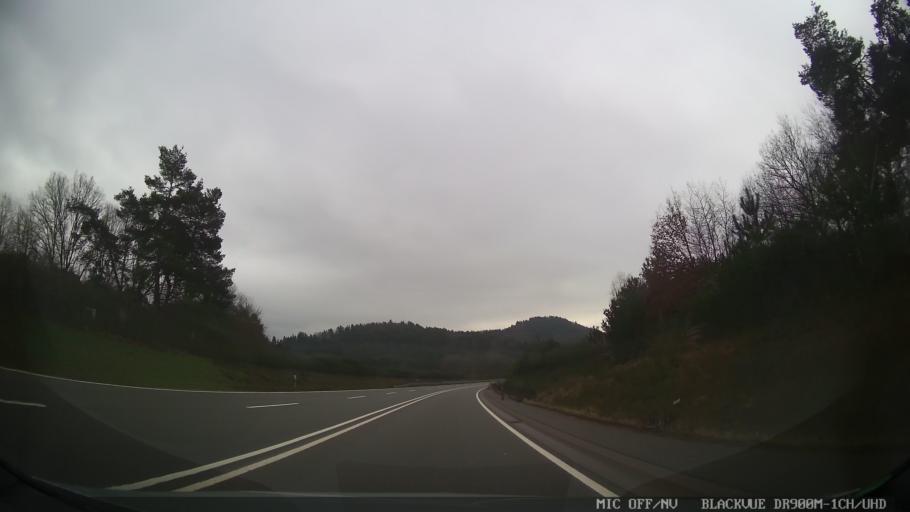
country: DE
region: Saarland
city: Merzig
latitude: 49.4751
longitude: 6.6300
